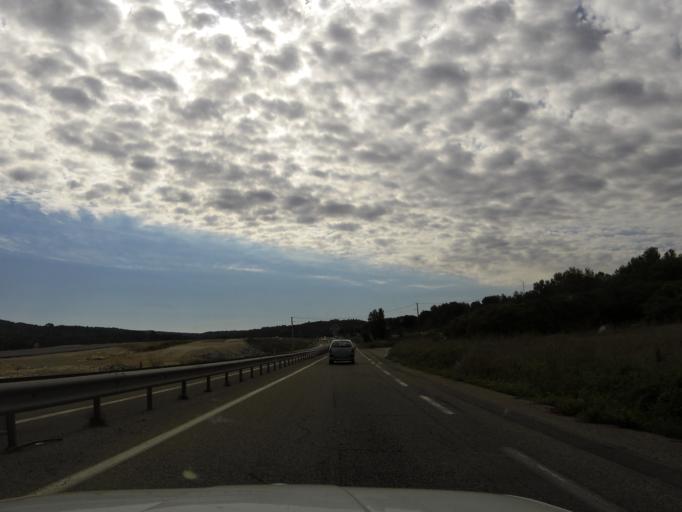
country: FR
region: Languedoc-Roussillon
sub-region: Departement du Gard
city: La Calmette
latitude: 43.9048
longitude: 4.2796
